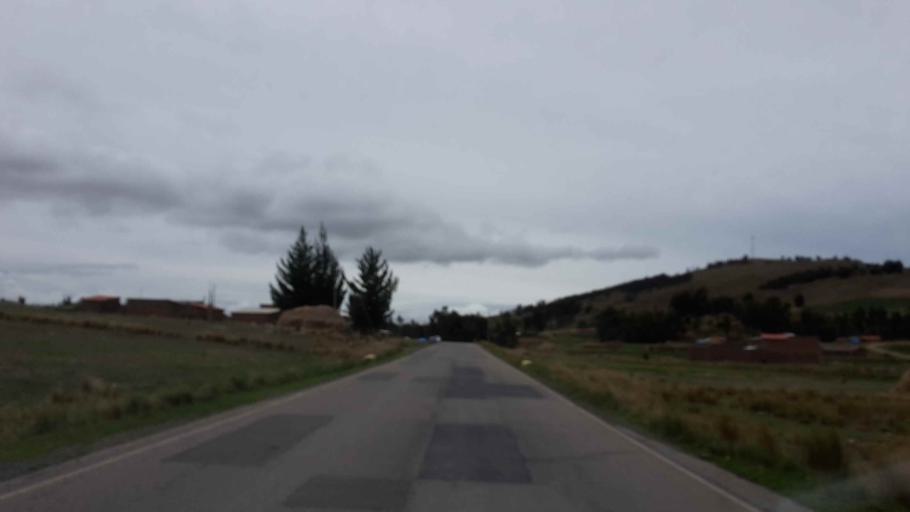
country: BO
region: Cochabamba
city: Arani
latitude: -17.4807
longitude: -65.6195
